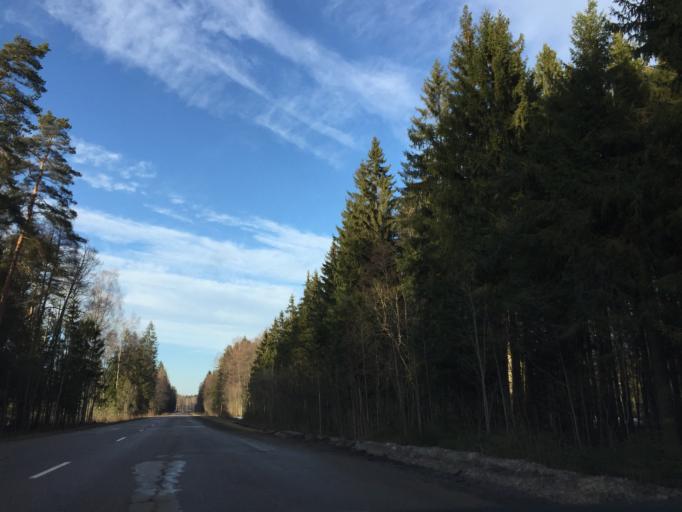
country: LV
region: Kekava
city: Balozi
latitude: 56.7419
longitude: 24.1084
